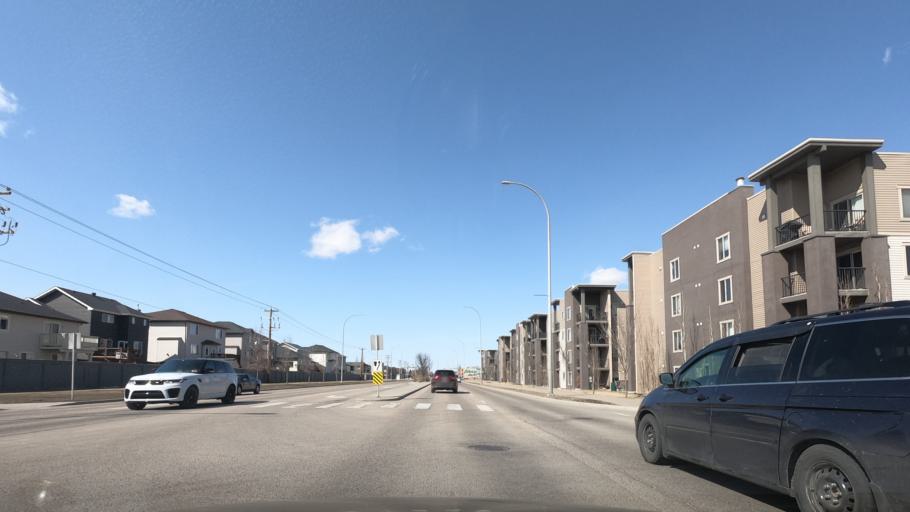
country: CA
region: Alberta
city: Airdrie
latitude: 51.2877
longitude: -114.0252
